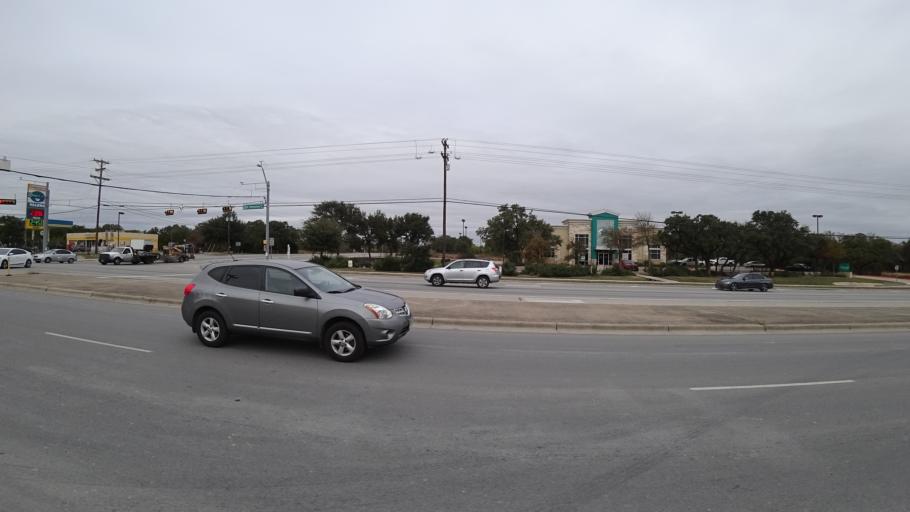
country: US
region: Texas
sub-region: Williamson County
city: Cedar Park
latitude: 30.5178
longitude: -97.8396
